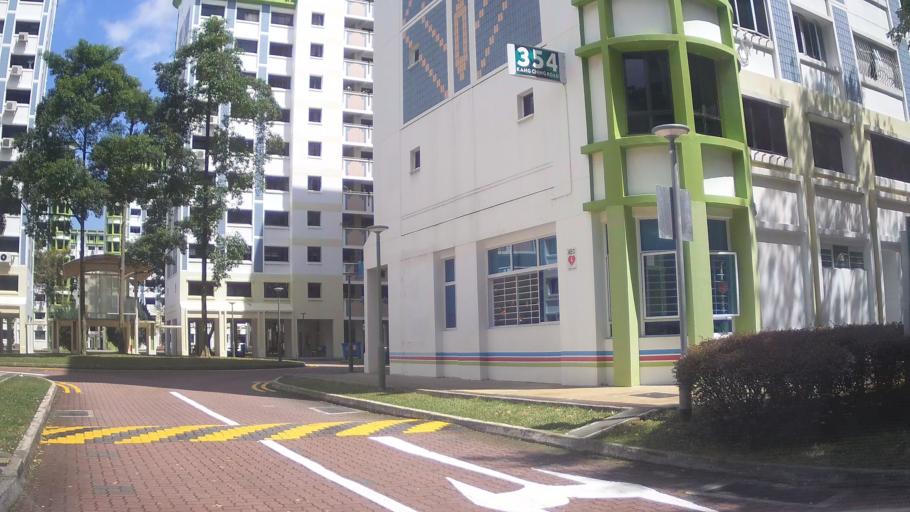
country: MY
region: Johor
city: Johor Bahru
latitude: 1.3396
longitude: 103.7210
